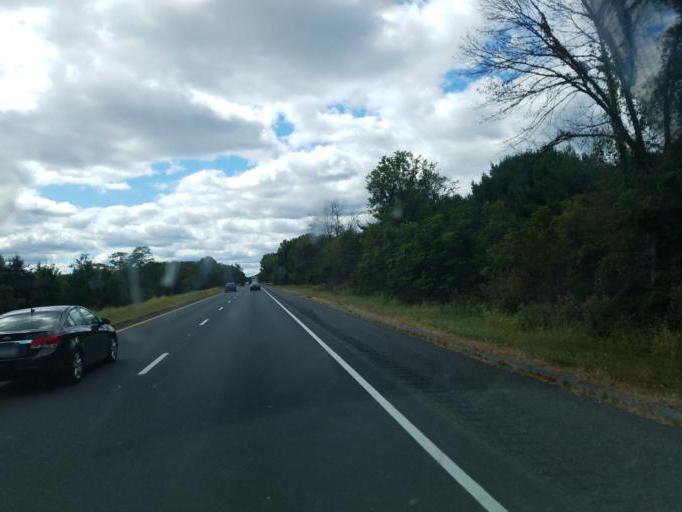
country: US
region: Maryland
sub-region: Washington County
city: Wilson-Conococheague
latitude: 39.6374
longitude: -77.9551
